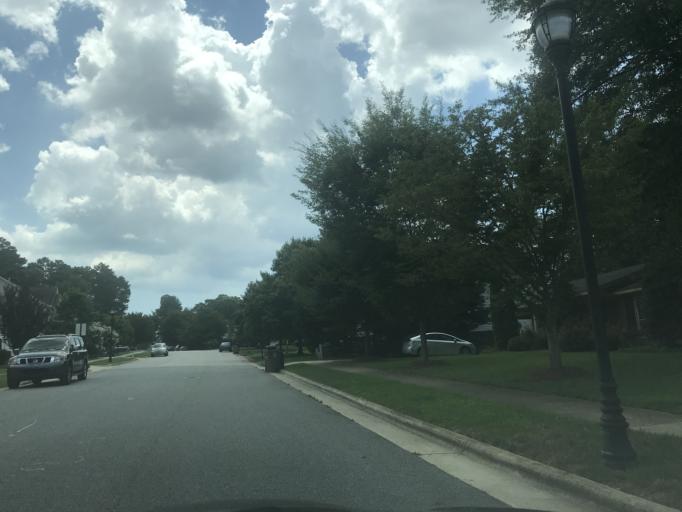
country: US
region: North Carolina
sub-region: Wake County
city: Wake Forest
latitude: 35.9586
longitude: -78.5260
